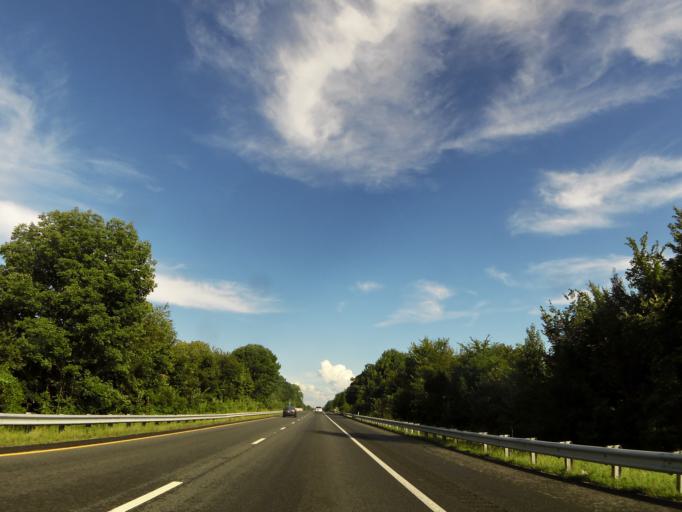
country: US
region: Tennessee
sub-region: Cheatham County
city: Pleasant View
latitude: 36.4876
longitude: -87.1618
